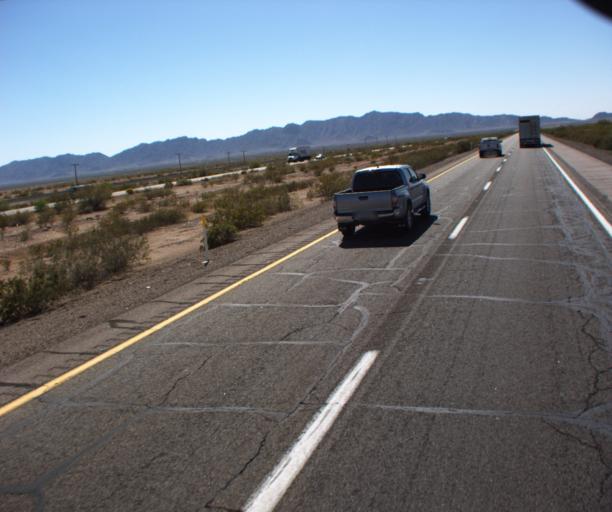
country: US
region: Arizona
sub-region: Yuma County
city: Wellton
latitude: 32.7607
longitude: -113.6364
